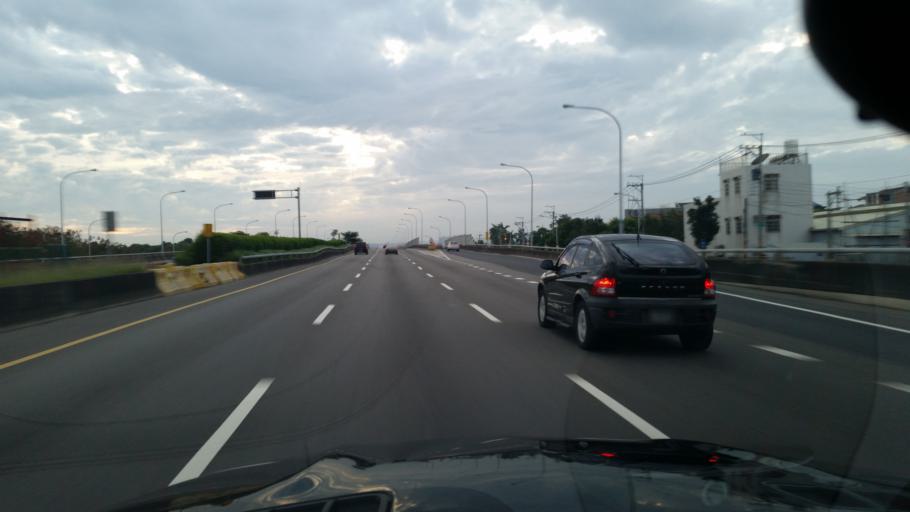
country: TW
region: Taiwan
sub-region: Taichung City
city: Taichung
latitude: 24.1979
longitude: 120.6513
